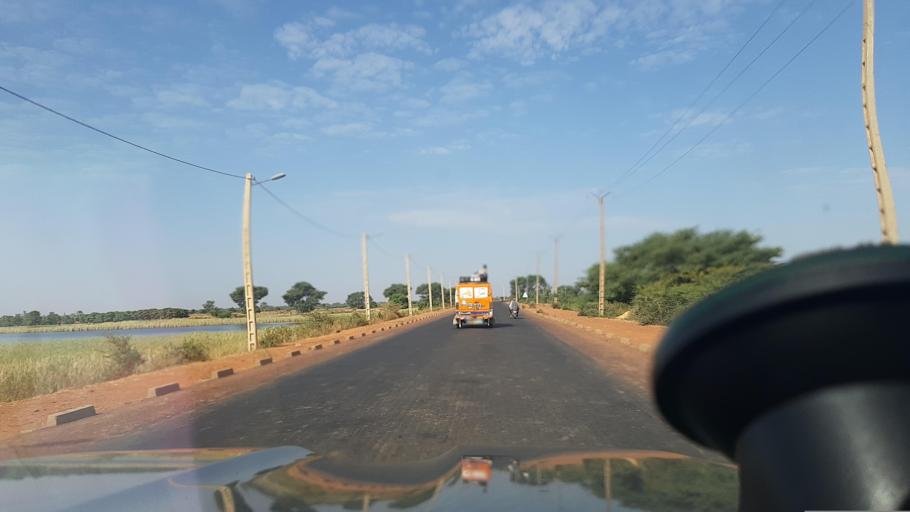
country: ML
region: Segou
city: Markala
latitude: 13.6849
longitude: -6.0953
